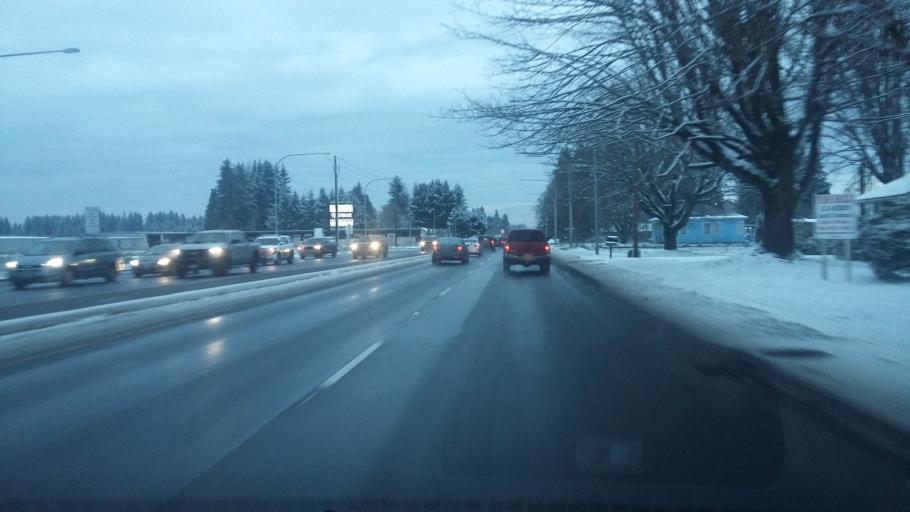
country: US
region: Washington
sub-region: Clark County
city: Brush Prairie
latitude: 45.7085
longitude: -122.5526
